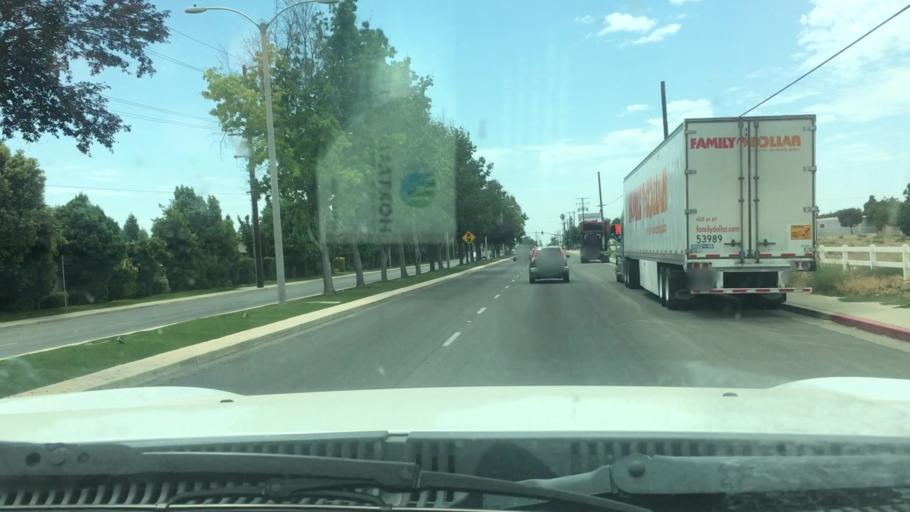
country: US
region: California
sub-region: Tulare County
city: Porterville
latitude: 36.0658
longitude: -119.0675
